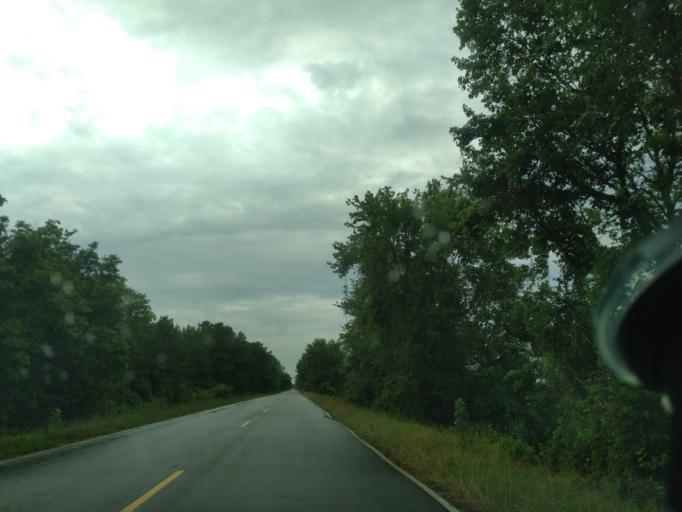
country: US
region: North Carolina
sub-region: Washington County
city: Plymouth
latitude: 35.8410
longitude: -76.5460
